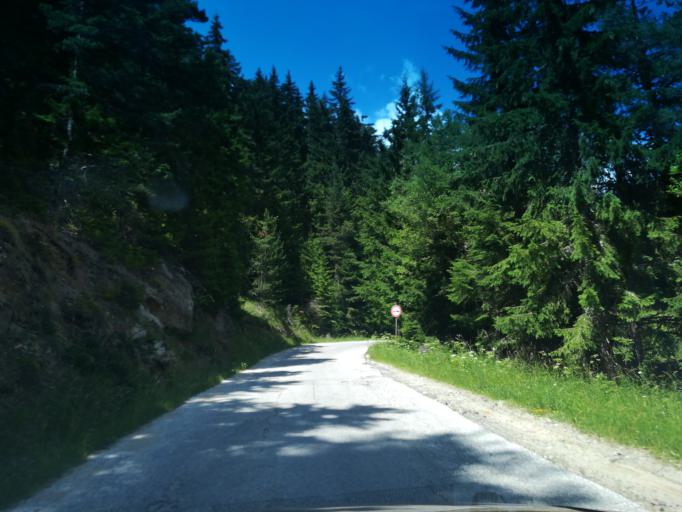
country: BG
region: Smolyan
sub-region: Obshtina Chepelare
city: Chepelare
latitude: 41.6879
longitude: 24.7718
